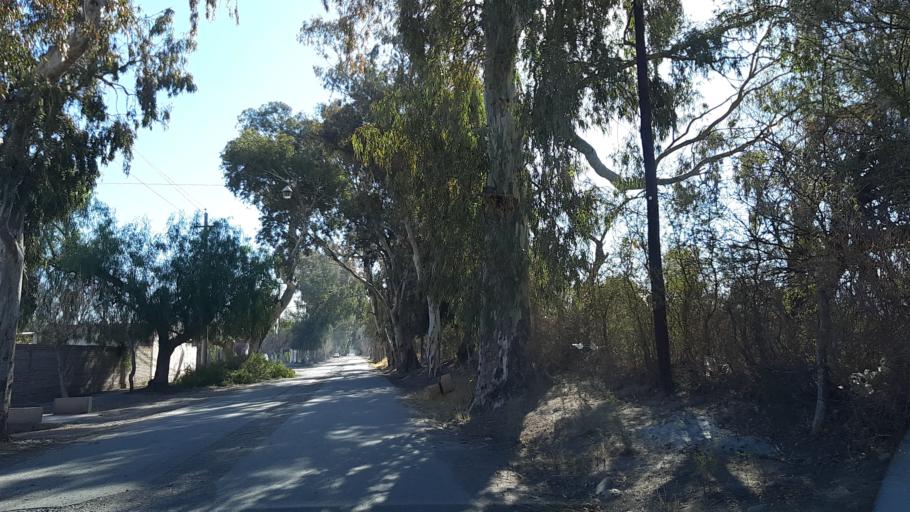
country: AR
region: San Juan
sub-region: Departamento de Zonda
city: Zonda
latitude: -31.5497
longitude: -68.7272
